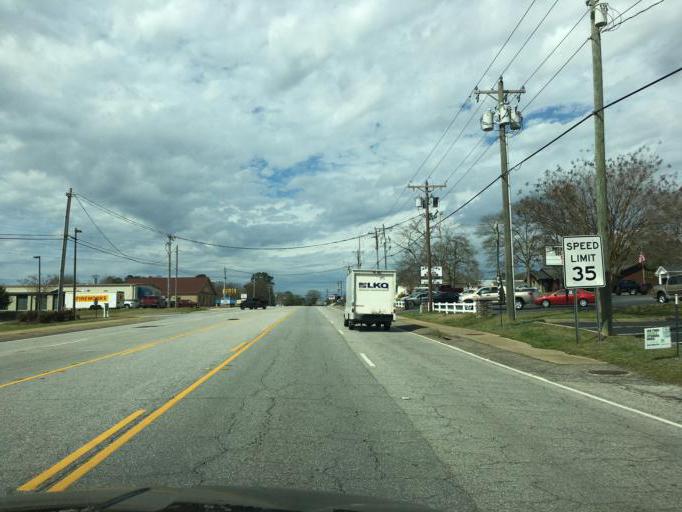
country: US
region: South Carolina
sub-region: Greenville County
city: Fountain Inn
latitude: 34.7015
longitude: -82.2170
